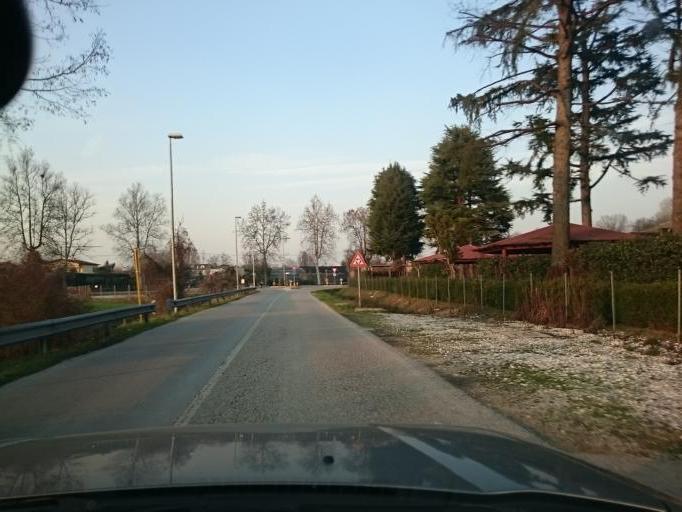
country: IT
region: Veneto
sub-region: Provincia di Padova
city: Mandriola-Sant'Agostino
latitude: 45.3658
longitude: 11.8248
